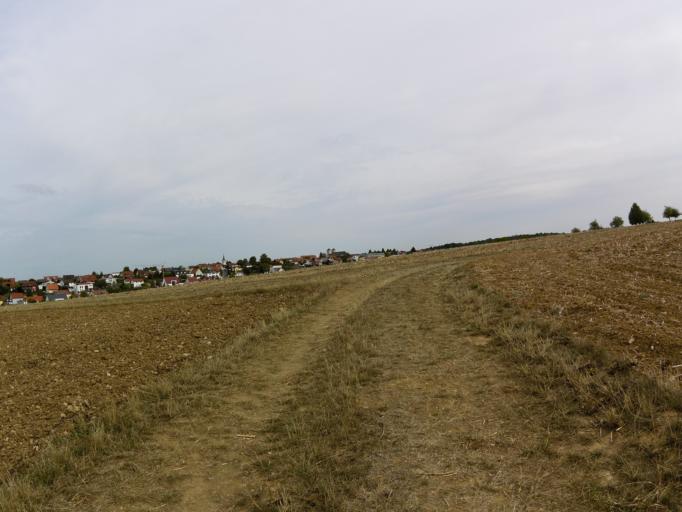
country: DE
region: Bavaria
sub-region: Regierungsbezirk Unterfranken
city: Waldbuttelbrunn
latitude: 49.7799
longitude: 9.8366
